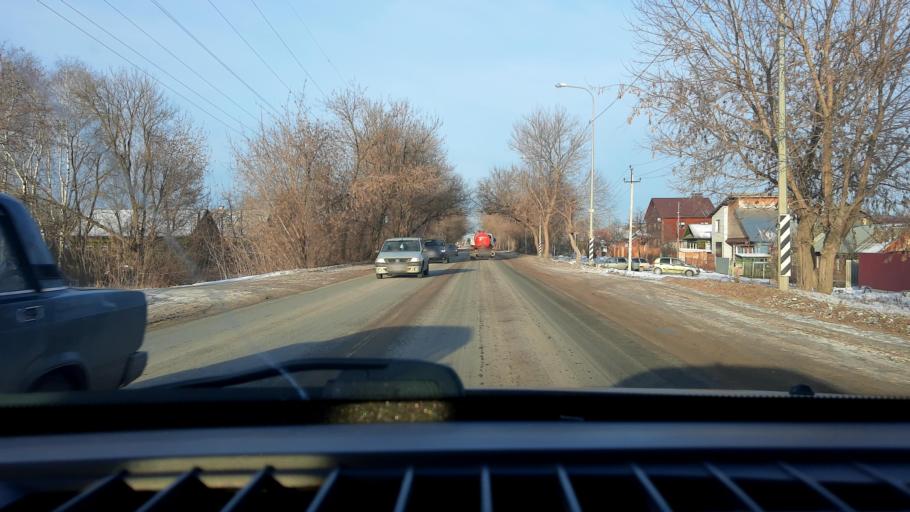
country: RU
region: Nizjnij Novgorod
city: Bor
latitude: 56.3665
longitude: 44.0705
